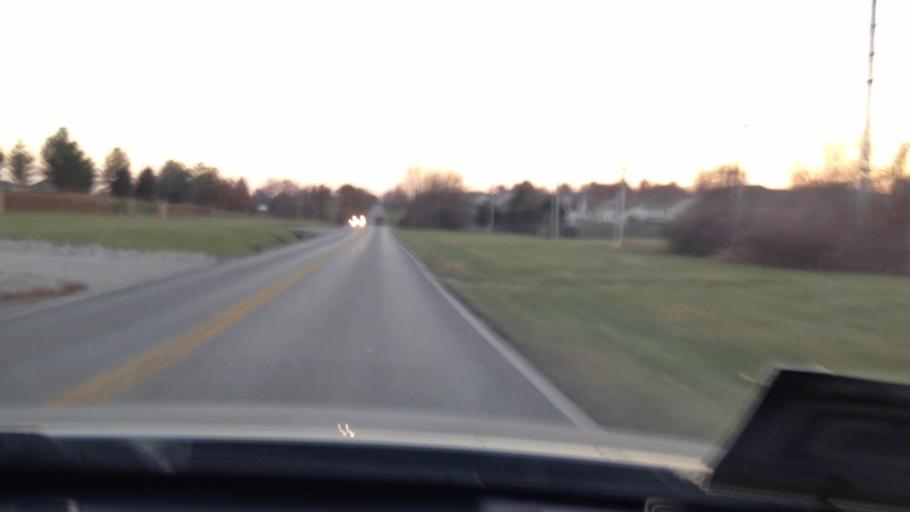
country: US
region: Missouri
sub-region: Clay County
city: Gladstone
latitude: 39.2820
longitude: -94.5571
